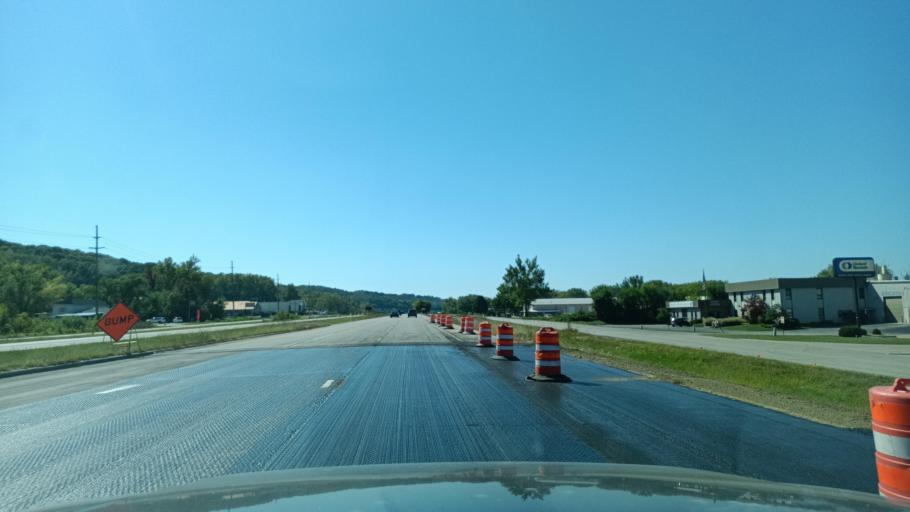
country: US
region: Illinois
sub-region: Peoria County
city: North Peoria
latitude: 40.7055
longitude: -89.5353
